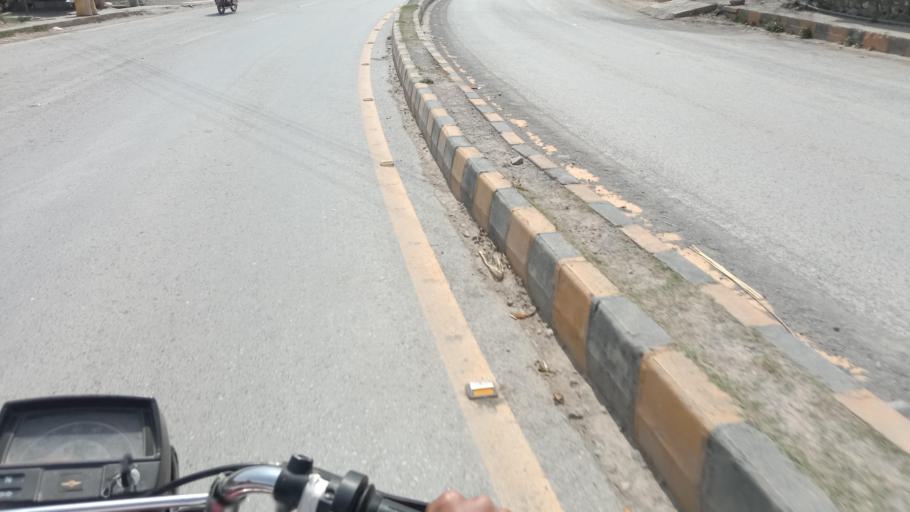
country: PK
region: Khyber Pakhtunkhwa
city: Abbottabad
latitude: 34.1524
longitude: 73.2672
